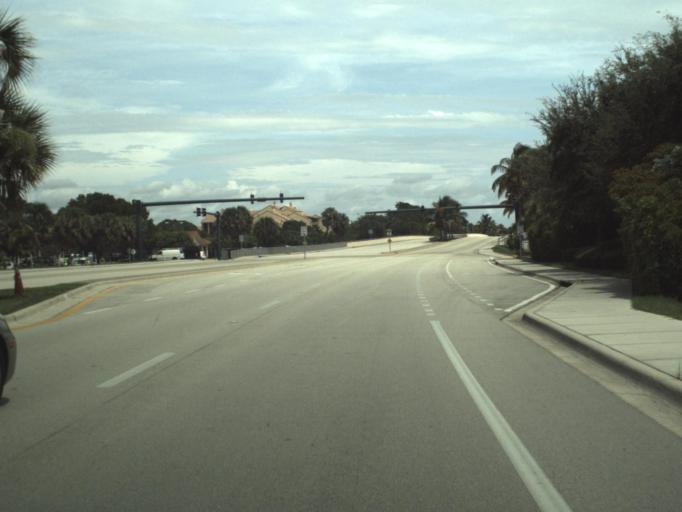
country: US
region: Florida
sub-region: Palm Beach County
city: Jupiter
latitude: 26.9395
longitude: -80.0837
